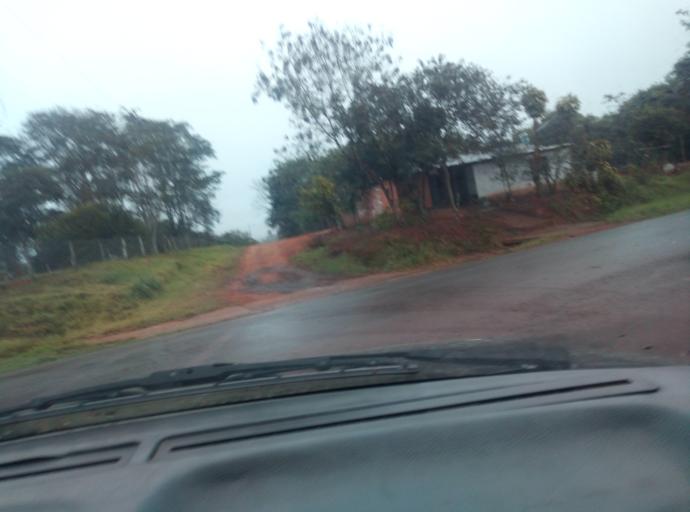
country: PY
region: Caaguazu
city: Carayao
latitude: -25.1903
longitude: -56.3111
